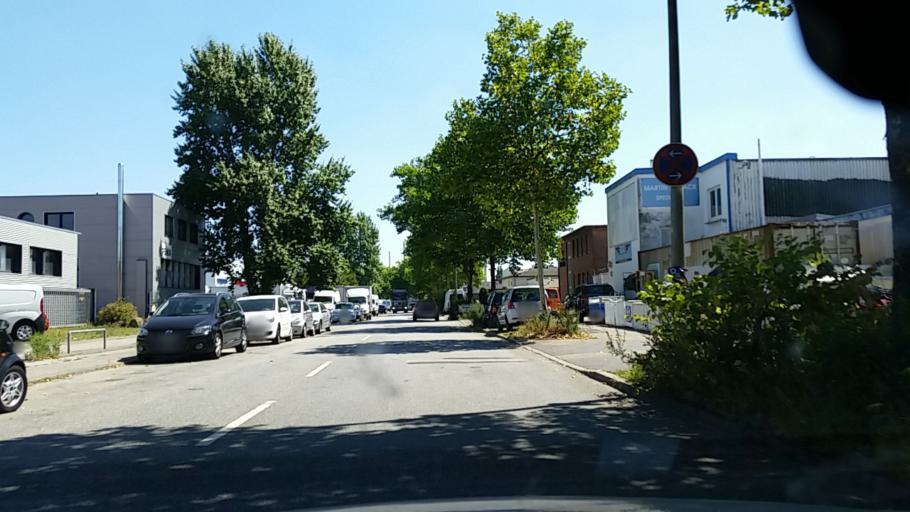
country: DE
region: Hamburg
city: Rothenburgsort
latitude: 53.5353
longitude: 10.0603
